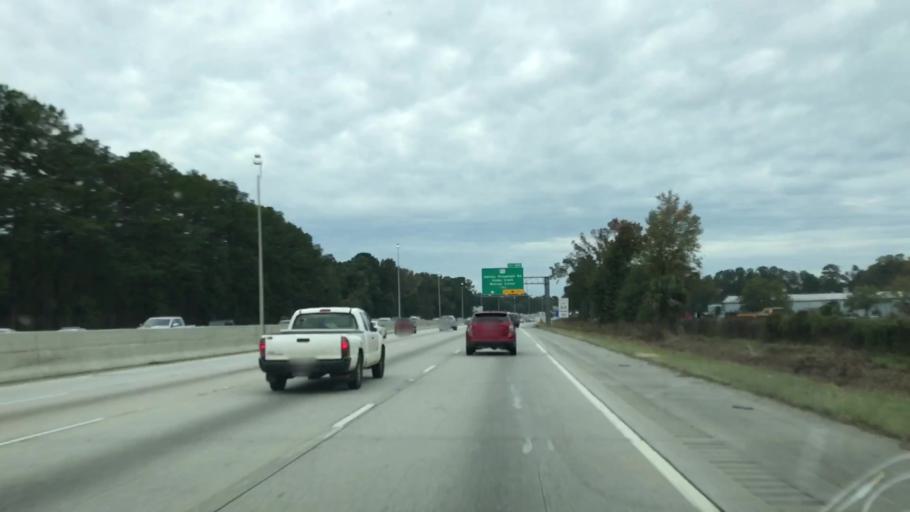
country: US
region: South Carolina
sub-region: Berkeley County
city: Hanahan
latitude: 32.9166
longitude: -80.0323
